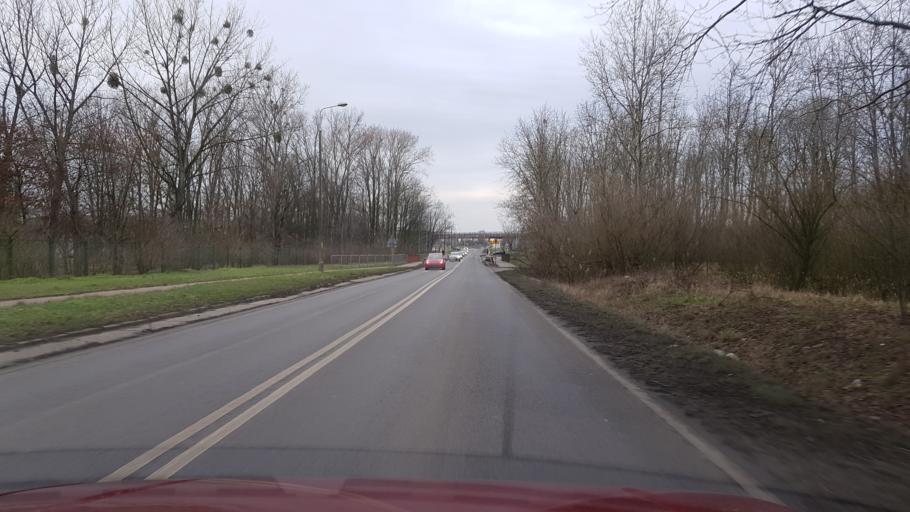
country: PL
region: West Pomeranian Voivodeship
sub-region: Powiat policki
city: Police
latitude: 53.5686
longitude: 14.5572
